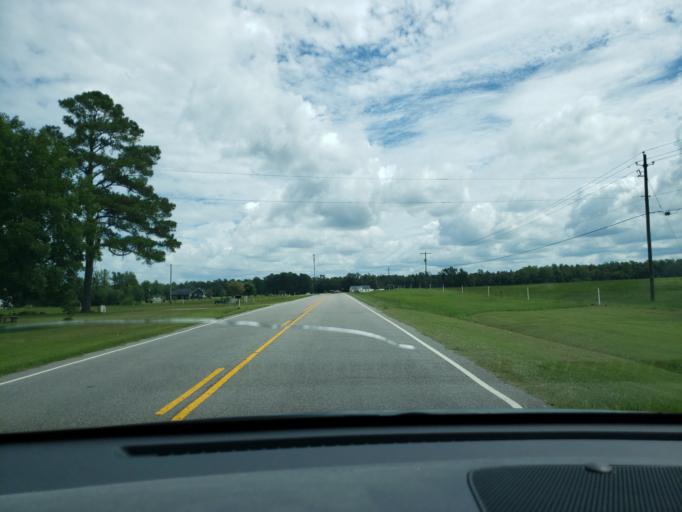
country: US
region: North Carolina
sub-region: Columbus County
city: Tabor City
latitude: 34.1877
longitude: -78.7810
